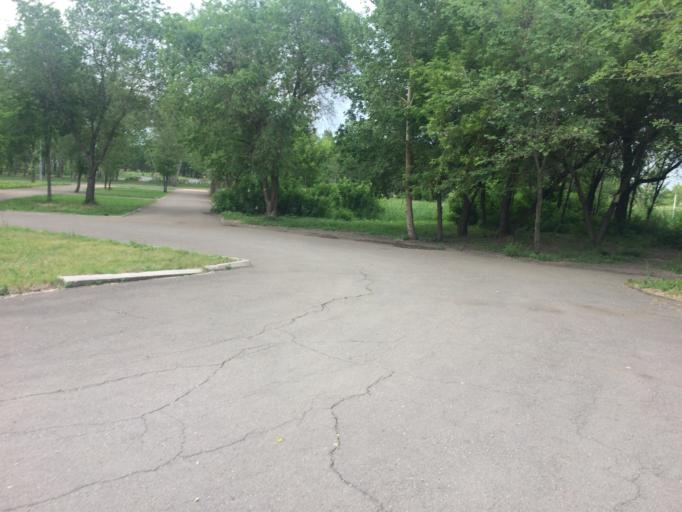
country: RU
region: Chelyabinsk
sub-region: Gorod Magnitogorsk
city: Magnitogorsk
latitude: 53.4004
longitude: 58.9924
